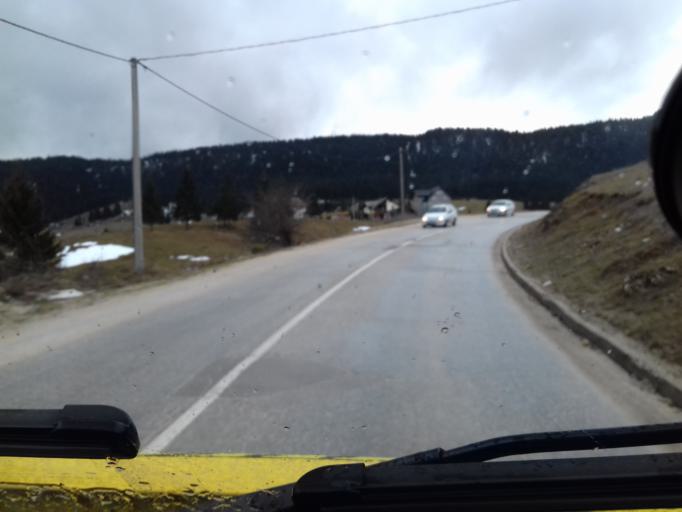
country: BA
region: Federation of Bosnia and Herzegovina
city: Turbe
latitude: 44.3087
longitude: 17.5486
